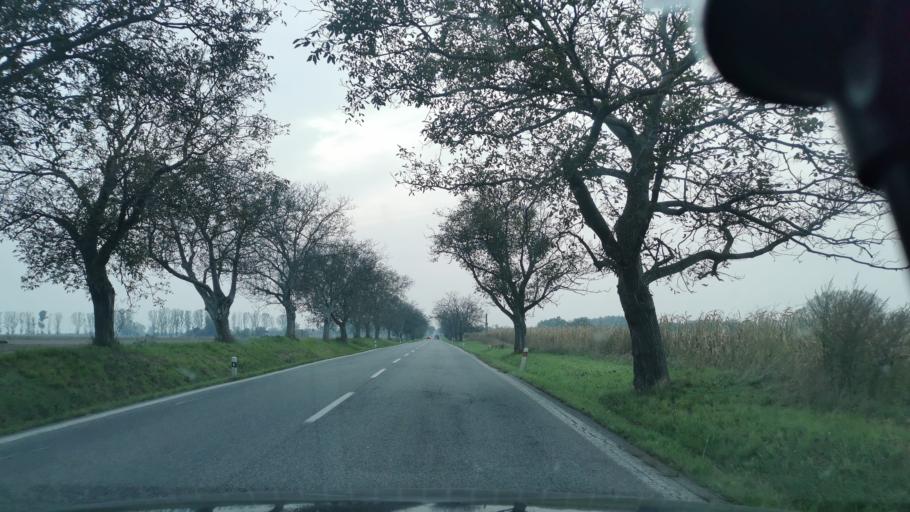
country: SK
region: Trnavsky
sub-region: Okres Skalica
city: Holic
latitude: 48.7983
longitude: 17.1442
